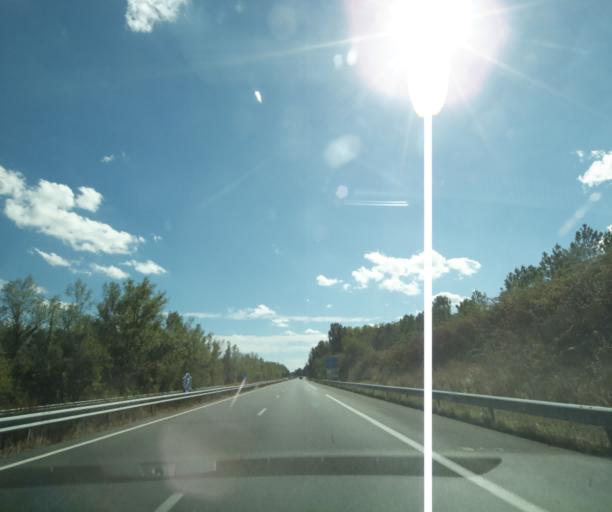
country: FR
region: Aquitaine
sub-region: Departement du Lot-et-Garonne
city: Damazan
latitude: 44.3519
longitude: 0.2493
